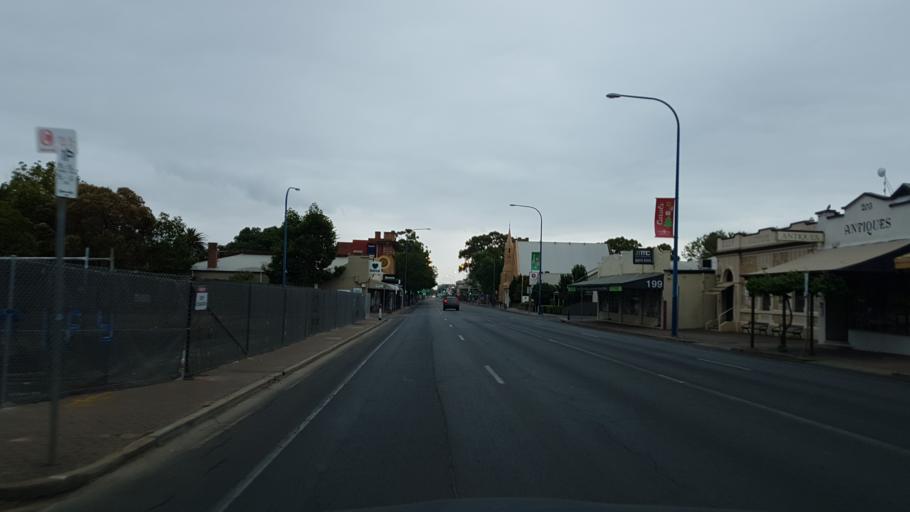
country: AU
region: South Australia
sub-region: Unley
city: Unley
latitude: -34.9533
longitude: 138.6075
